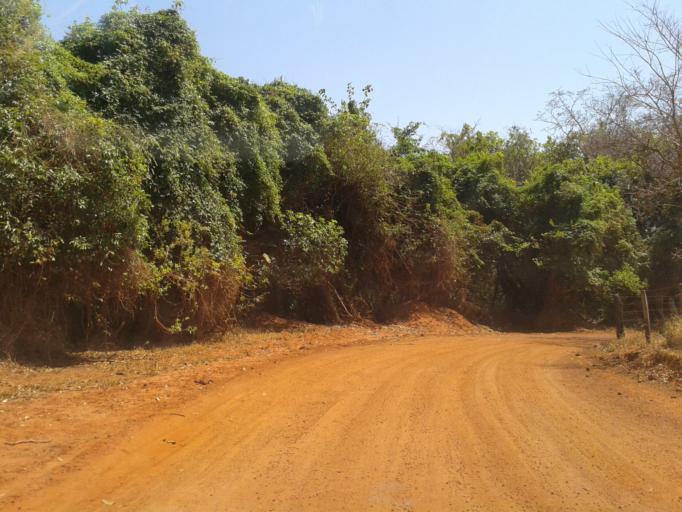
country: BR
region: Minas Gerais
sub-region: Ituiutaba
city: Ituiutaba
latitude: -19.0509
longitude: -49.3780
